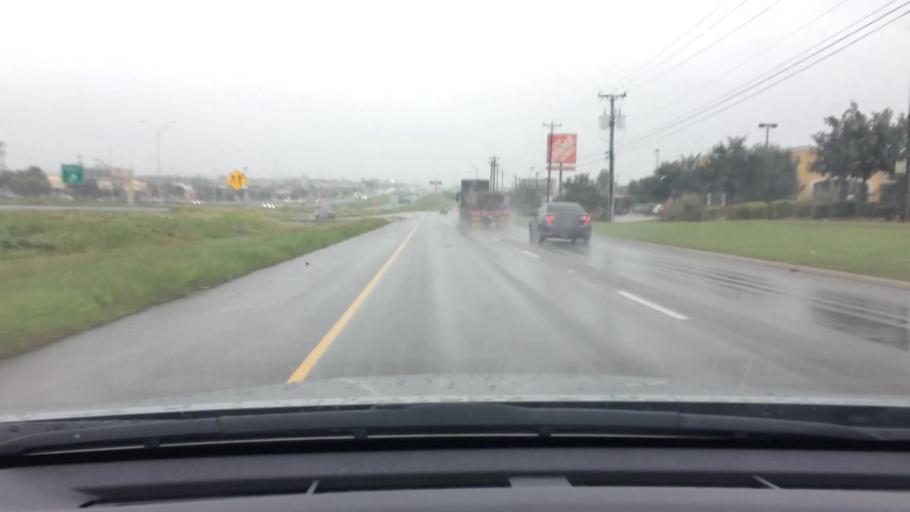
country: US
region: Texas
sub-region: Bexar County
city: Leon Valley
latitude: 29.4879
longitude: -98.7074
